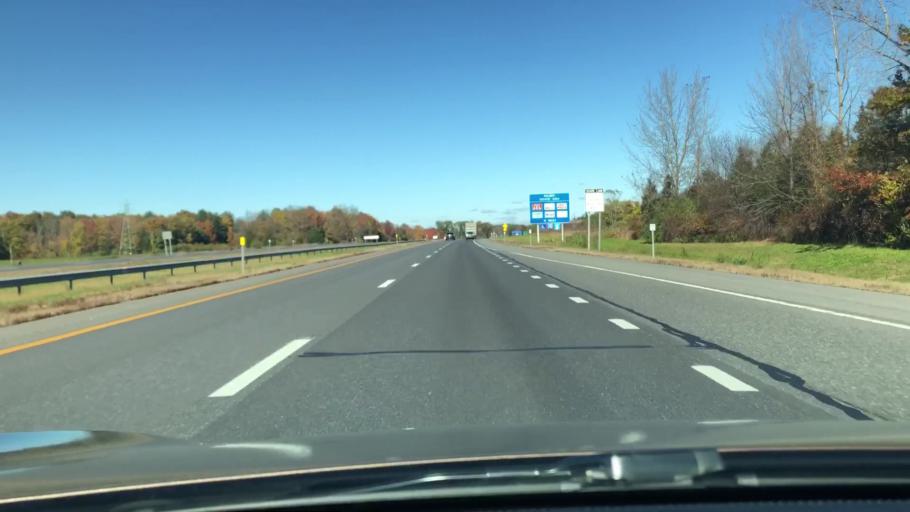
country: US
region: New York
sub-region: Ulster County
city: Saugerties South
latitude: 42.0589
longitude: -73.9821
